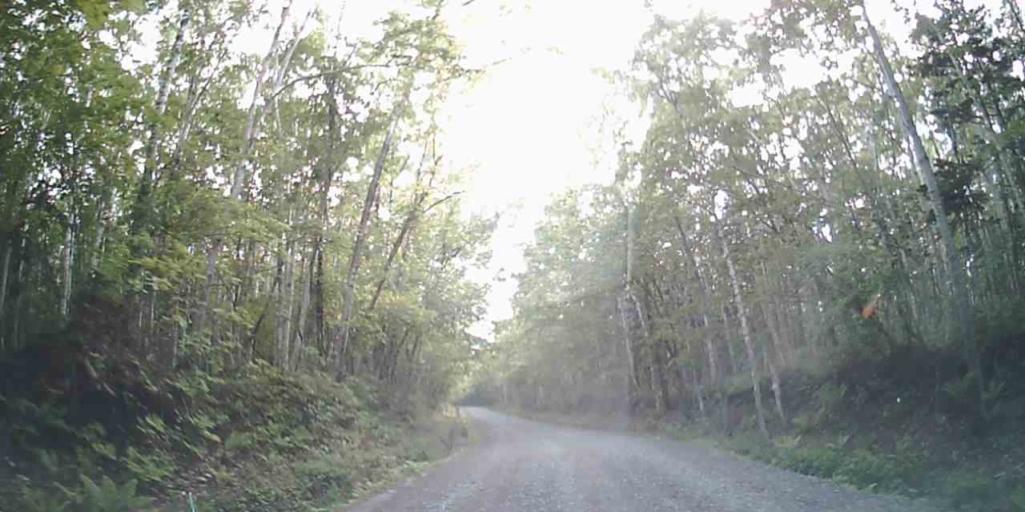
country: JP
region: Hokkaido
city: Shiraoi
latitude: 42.7142
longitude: 141.4031
